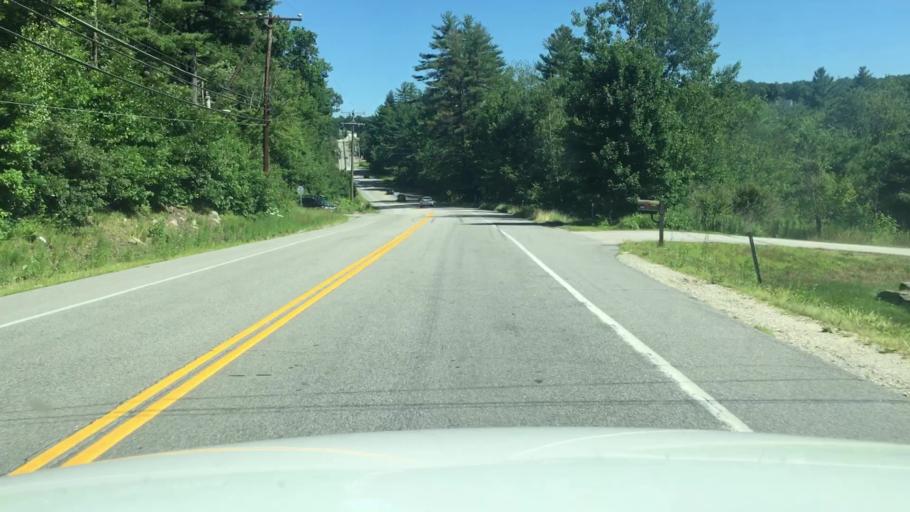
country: US
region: New Hampshire
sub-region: Merrimack County
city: South Hooksett
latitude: 43.0413
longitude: -71.4224
